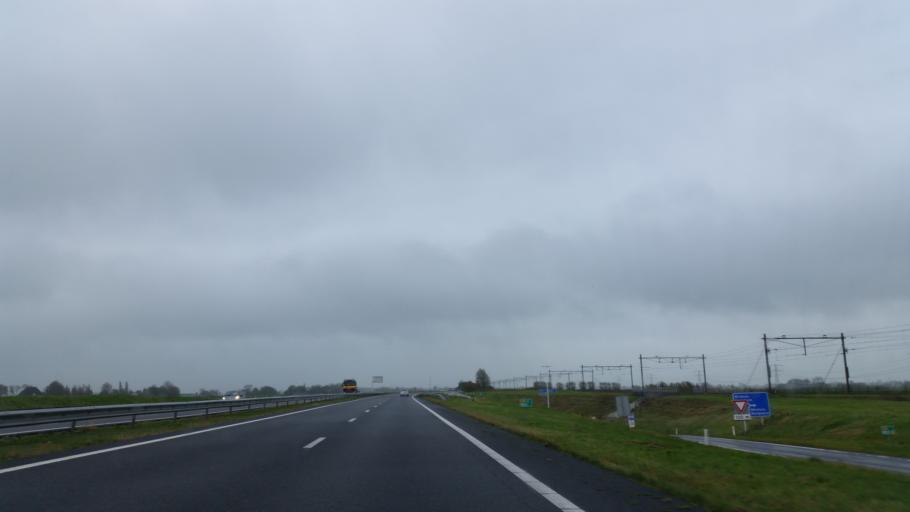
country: NL
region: Friesland
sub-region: Gemeente Leeuwarden
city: Wirdum
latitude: 53.1464
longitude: 5.7952
